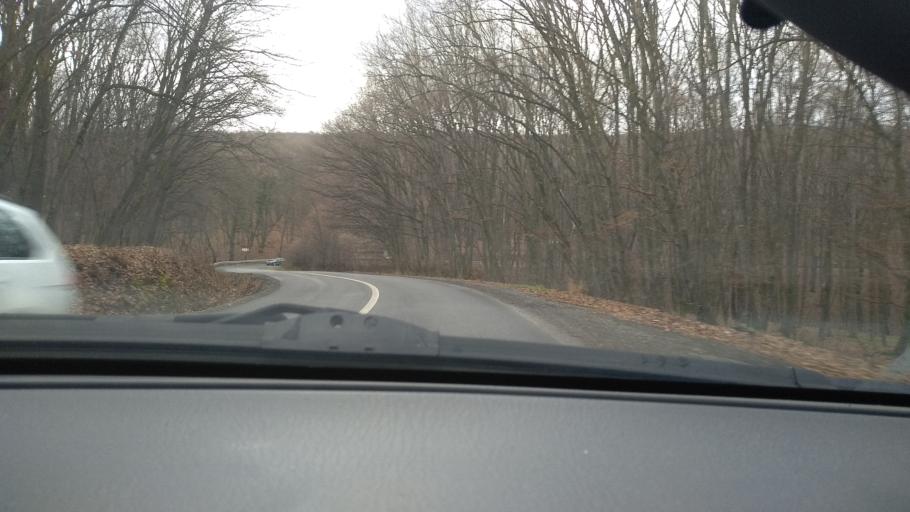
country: RO
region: Mures
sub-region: Comuna Pasareni
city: Pasareni
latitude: 46.5321
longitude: 24.6997
